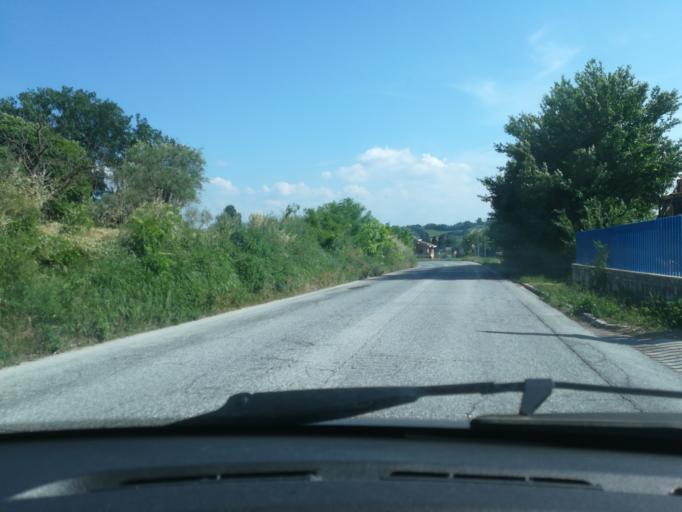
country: IT
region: The Marches
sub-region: Provincia di Macerata
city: Treia
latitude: 43.3052
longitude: 13.3128
